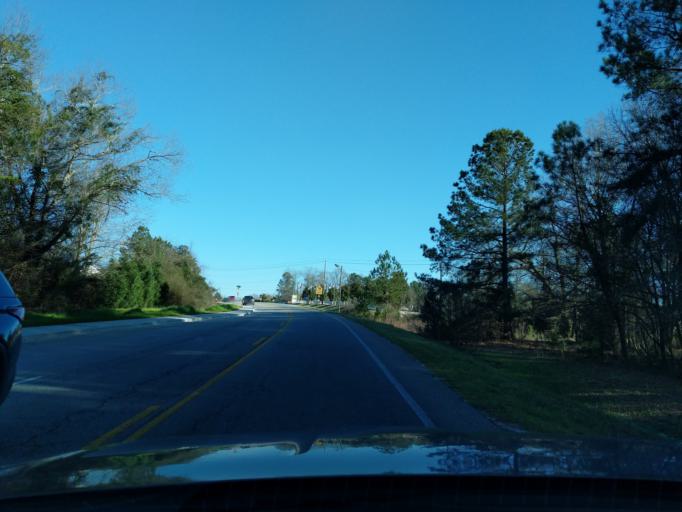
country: US
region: Georgia
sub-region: Columbia County
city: Grovetown
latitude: 33.4530
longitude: -82.2247
